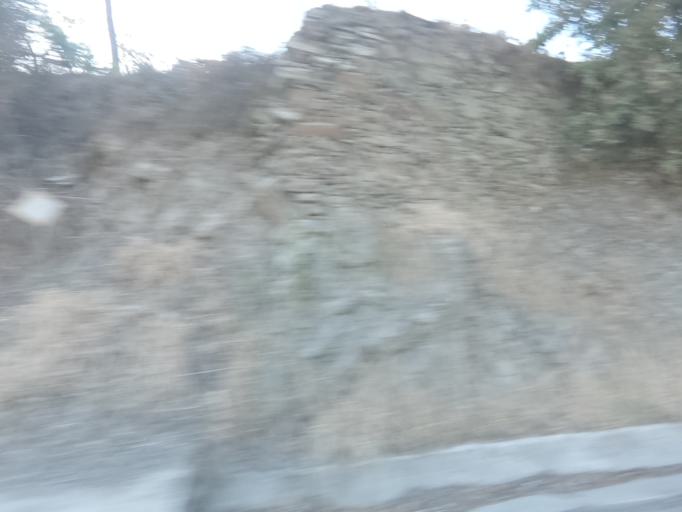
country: PT
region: Vila Real
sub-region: Peso da Regua
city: Godim
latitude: 41.1911
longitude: -7.8307
